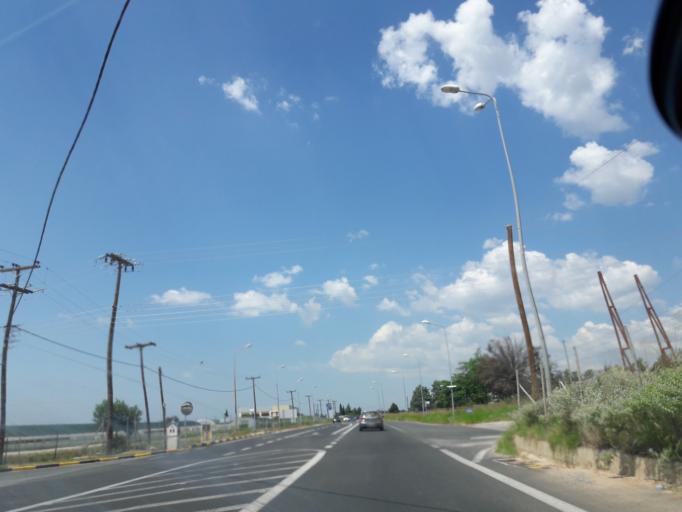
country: GR
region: Central Macedonia
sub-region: Nomos Thessalonikis
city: Agia Paraskevi
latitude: 40.5173
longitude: 23.0663
